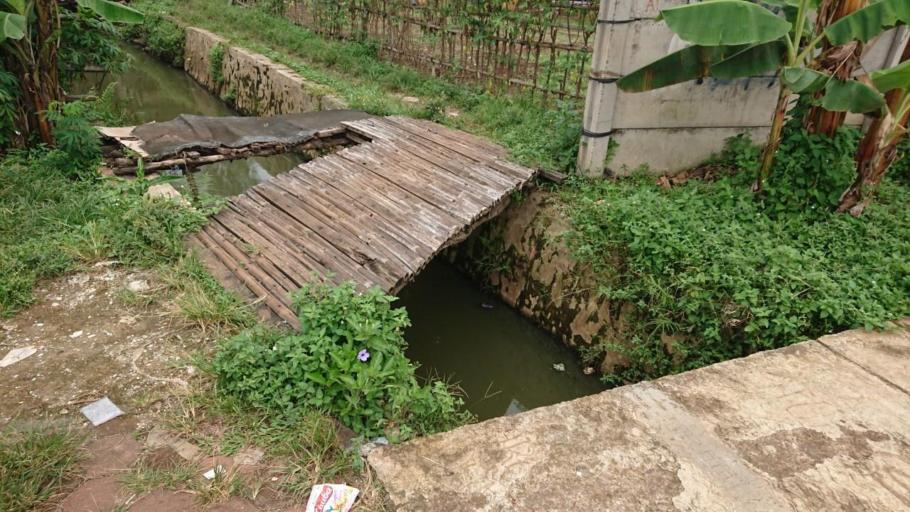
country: ID
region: West Java
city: Depok
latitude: -6.3520
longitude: 106.8561
